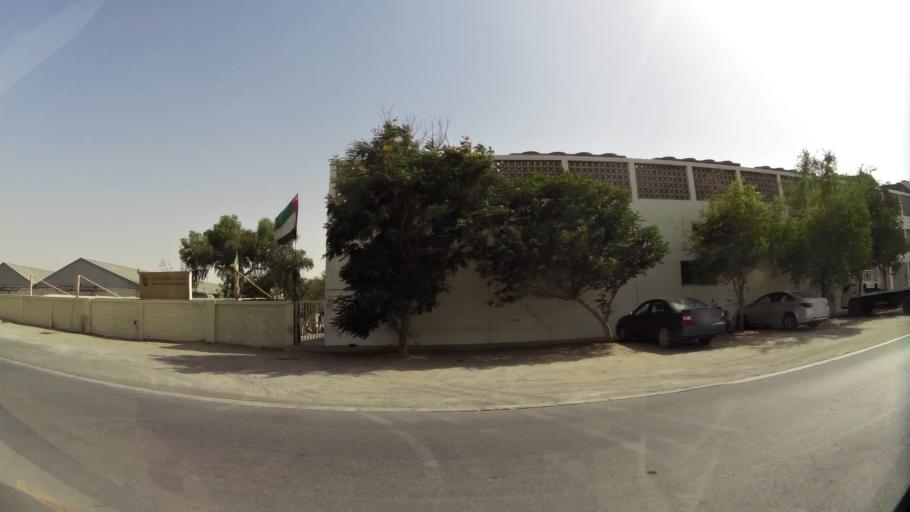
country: AE
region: Ash Shariqah
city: Sharjah
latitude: 25.2323
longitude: 55.3684
